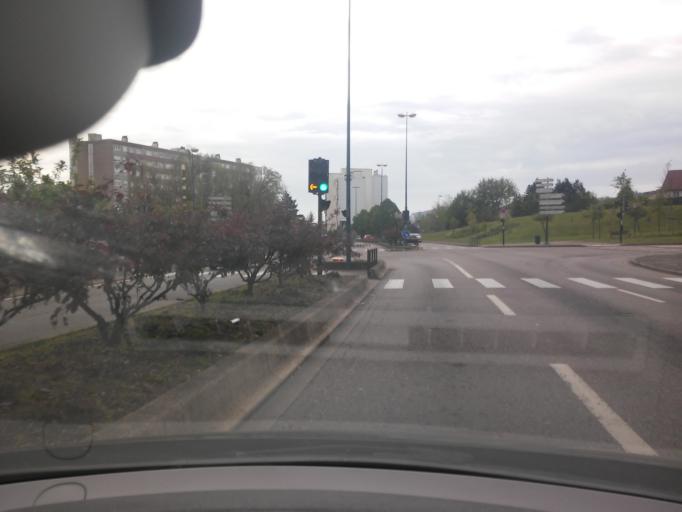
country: FR
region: Lorraine
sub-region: Departement de Meurthe-et-Moselle
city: Laxou
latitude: 48.6796
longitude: 6.1422
